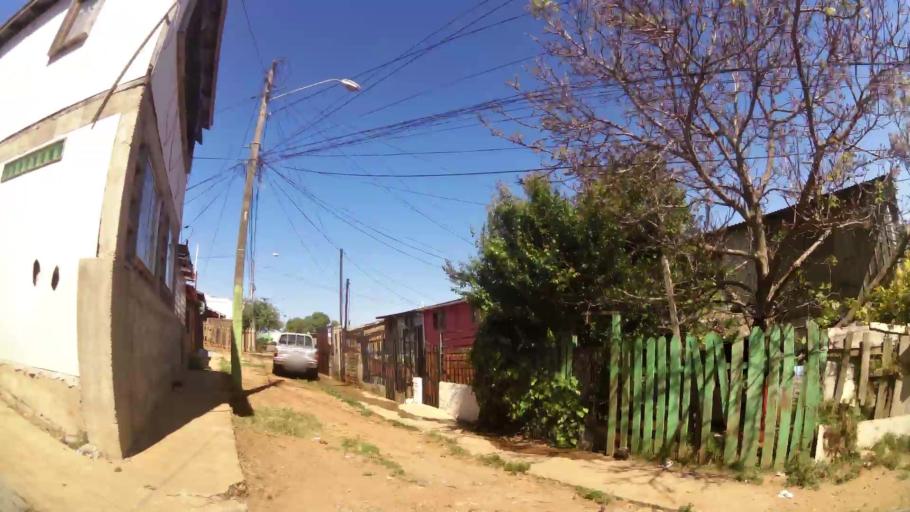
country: CL
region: Valparaiso
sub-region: Provincia de Valparaiso
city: Valparaiso
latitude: -33.0473
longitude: -71.6490
